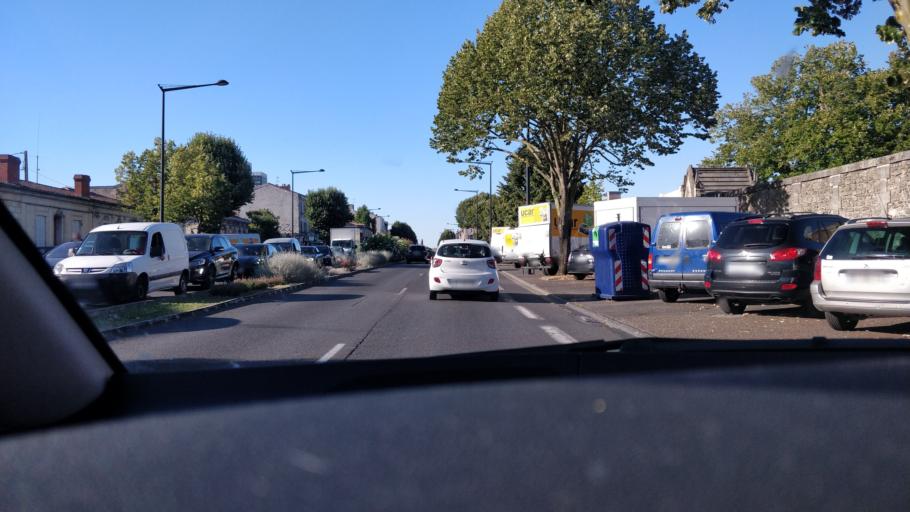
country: FR
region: Aquitaine
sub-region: Departement de la Gironde
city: Bordeaux
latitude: 44.8351
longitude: -0.5987
